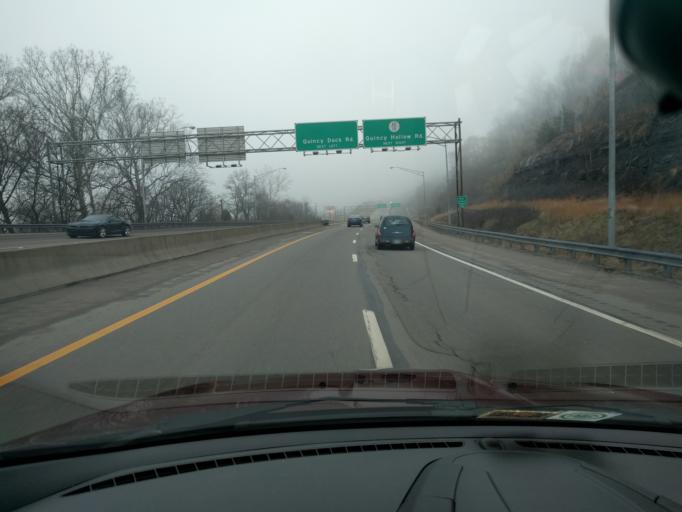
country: US
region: West Virginia
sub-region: Kanawha County
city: Chesapeake
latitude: 38.2016
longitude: -81.4999
